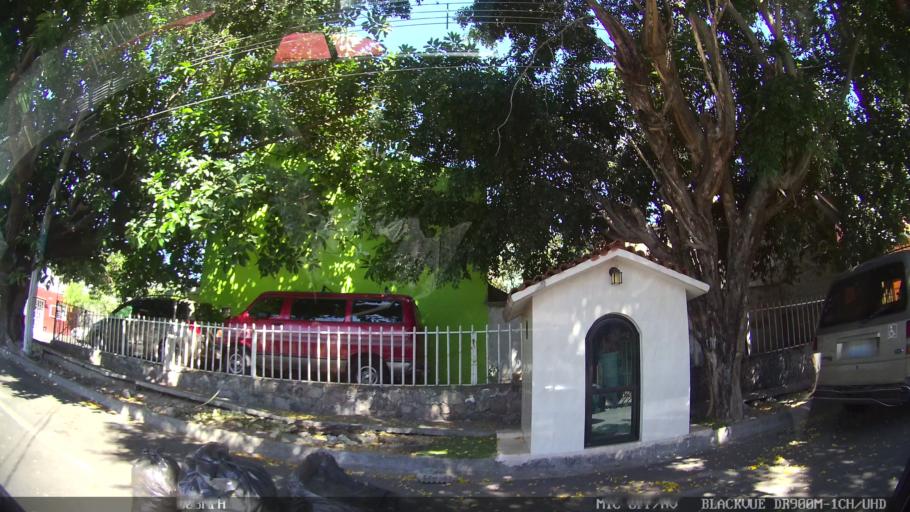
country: MX
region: Jalisco
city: Tlaquepaque
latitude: 20.6973
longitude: -103.2854
